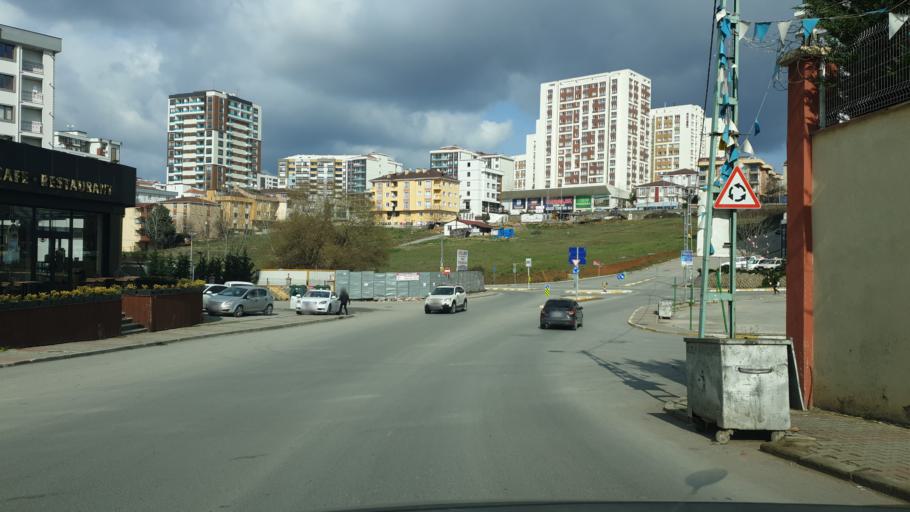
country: TR
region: Istanbul
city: Icmeler
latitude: 40.8715
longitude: 29.3235
